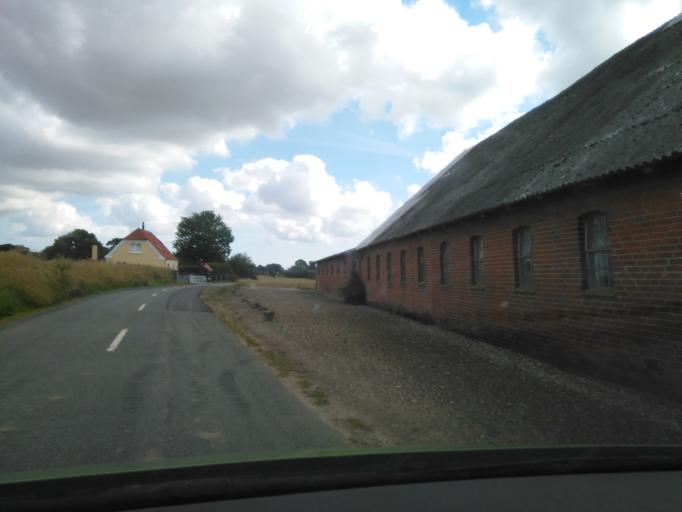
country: DK
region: Central Jutland
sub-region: Arhus Kommune
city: Solbjerg
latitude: 56.0054
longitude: 10.0467
